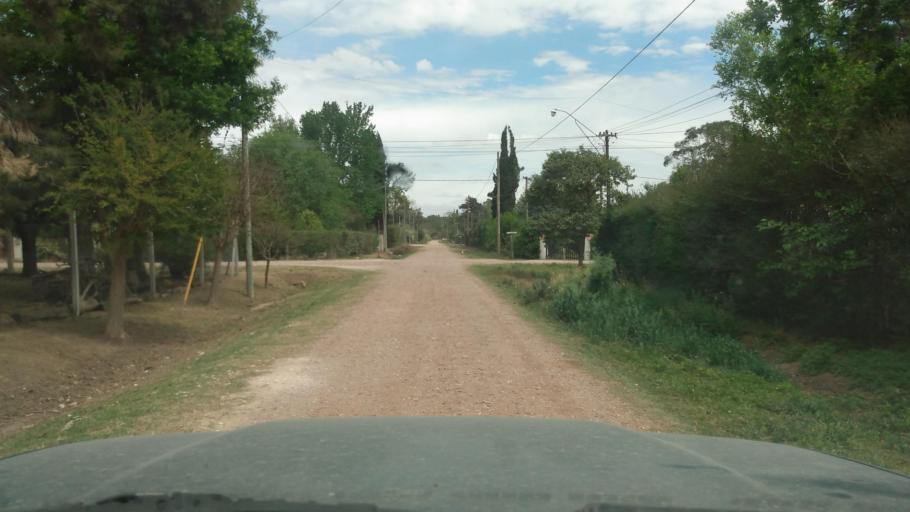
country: AR
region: Buenos Aires
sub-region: Partido de Lujan
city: Lujan
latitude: -34.5892
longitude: -59.1304
